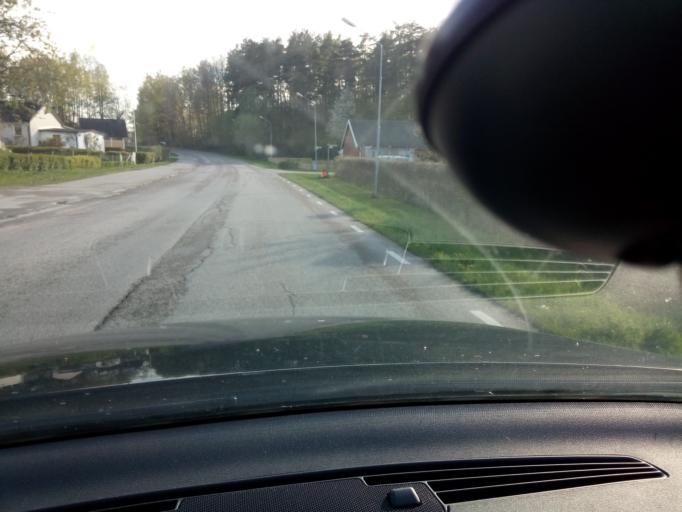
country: SE
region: Soedermanland
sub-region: Nykopings Kommun
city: Nykoping
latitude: 58.7780
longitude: 17.0892
